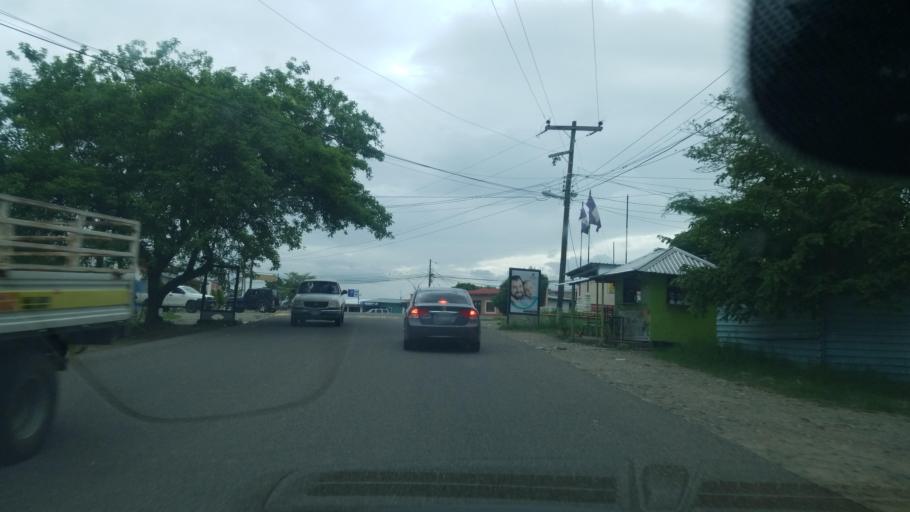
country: HN
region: Ocotepeque
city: Nueva Ocotepeque
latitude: 14.4414
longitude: -89.1843
